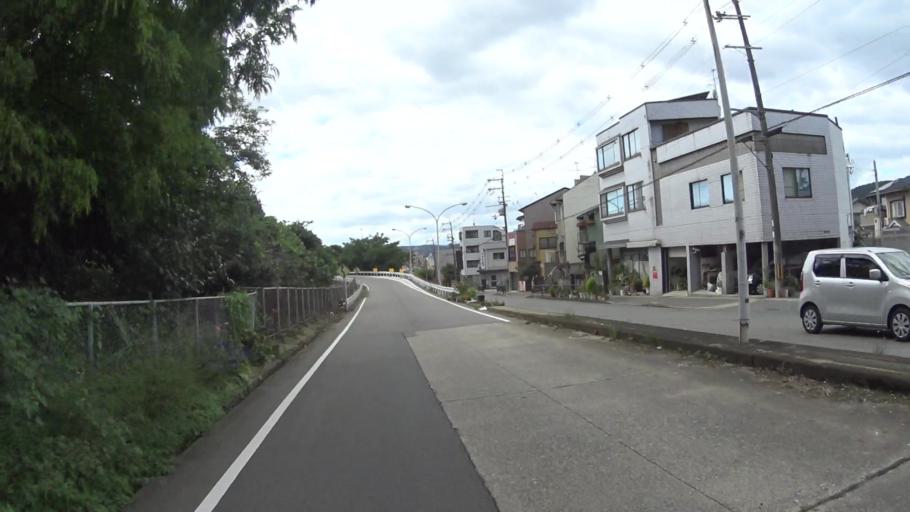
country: JP
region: Shiga Prefecture
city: Otsu-shi
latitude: 34.9905
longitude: 135.8293
